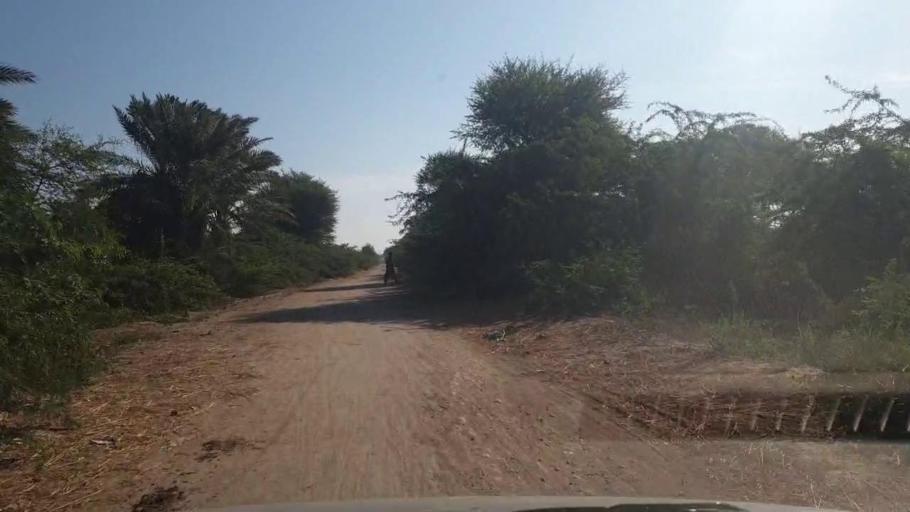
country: PK
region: Sindh
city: Rajo Khanani
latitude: 24.9716
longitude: 68.7676
